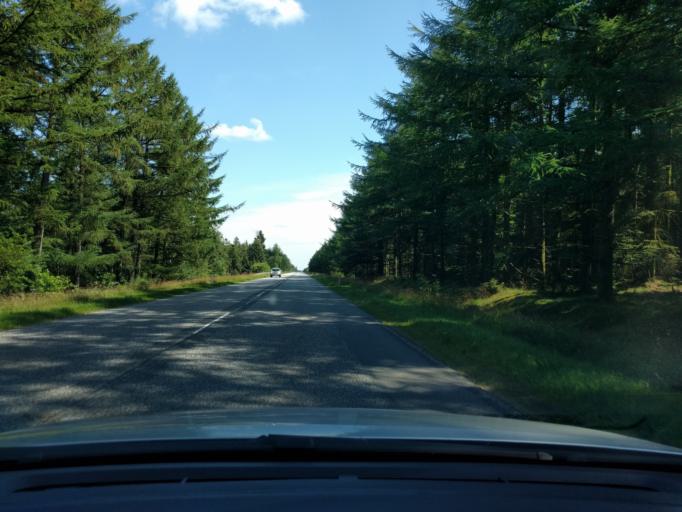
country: DK
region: Central Jutland
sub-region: Herning Kommune
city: Kibaek
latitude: 56.0554
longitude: 8.8896
